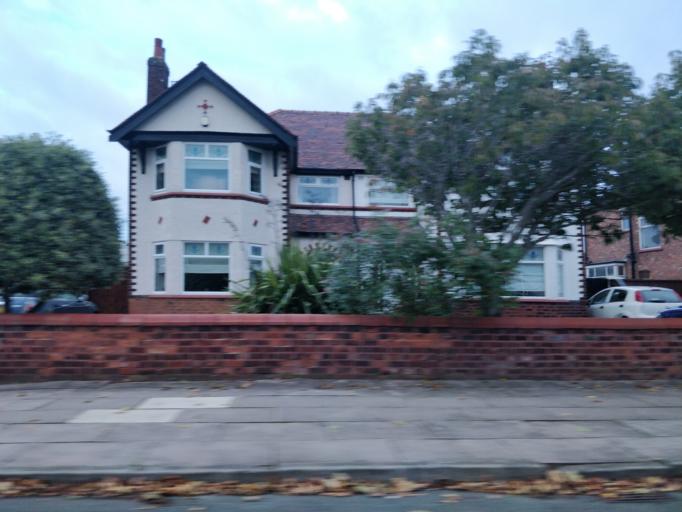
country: GB
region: England
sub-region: Sefton
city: Southport
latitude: 53.6630
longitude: -2.9709
